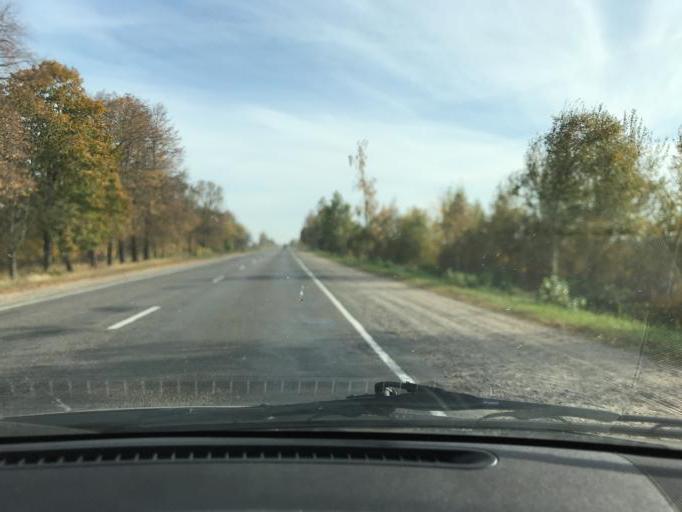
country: BY
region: Brest
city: Asnyezhytsy
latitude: 52.2155
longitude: 26.0406
